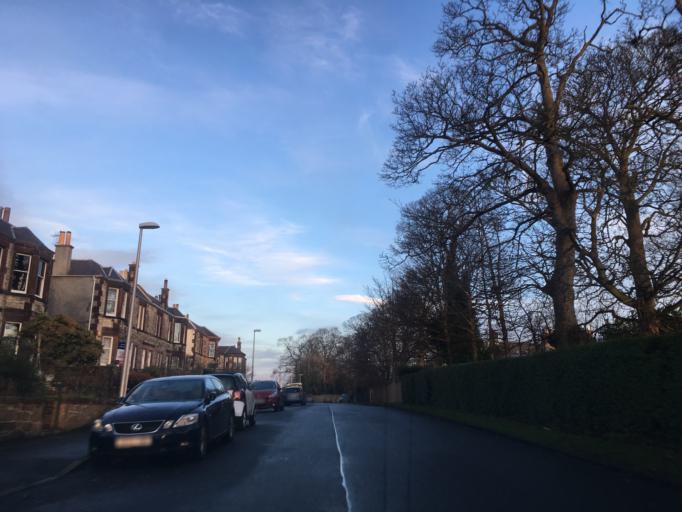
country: GB
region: Scotland
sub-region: Edinburgh
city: Colinton
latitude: 55.9485
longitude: -3.2439
